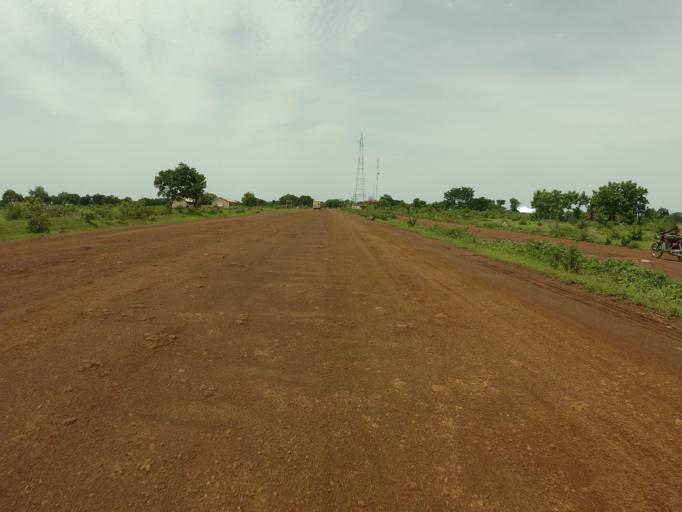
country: GH
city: Kpandae
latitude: 8.8751
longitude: 0.0409
